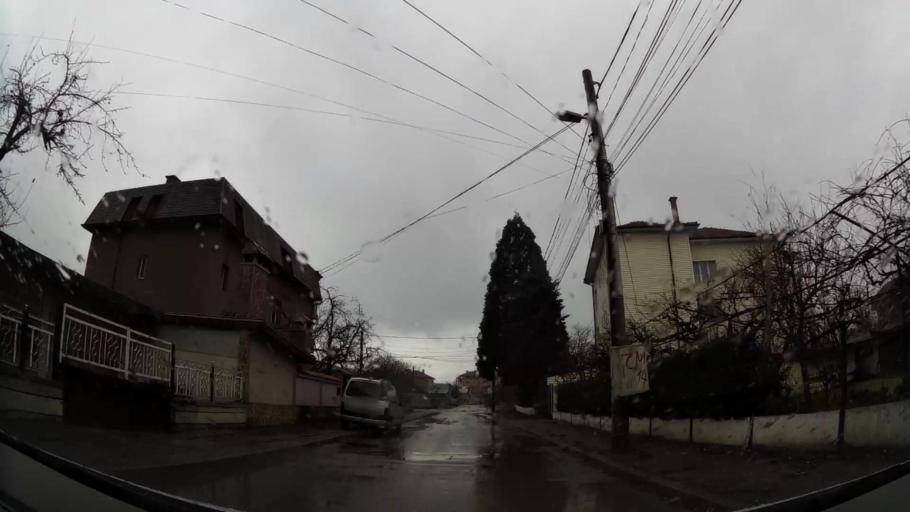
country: BG
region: Sofia-Capital
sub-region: Stolichna Obshtina
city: Sofia
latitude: 42.6310
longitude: 23.4124
